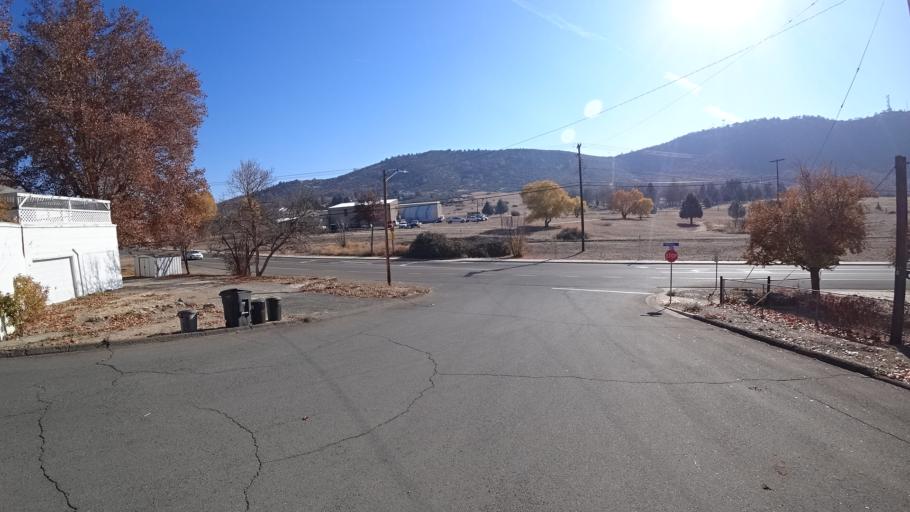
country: US
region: California
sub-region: Siskiyou County
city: Yreka
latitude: 41.7328
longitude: -122.6306
